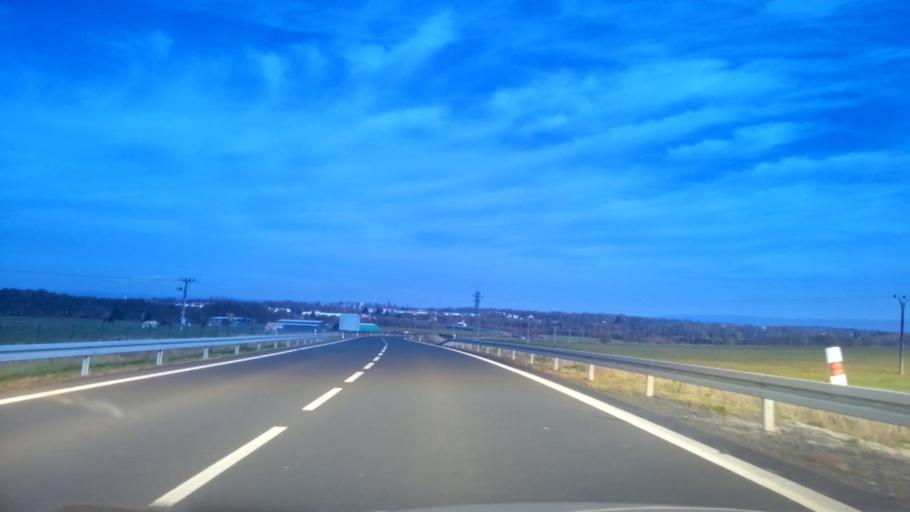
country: CZ
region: Karlovarsky
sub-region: Okres Cheb
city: Cheb
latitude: 50.0544
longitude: 12.3727
